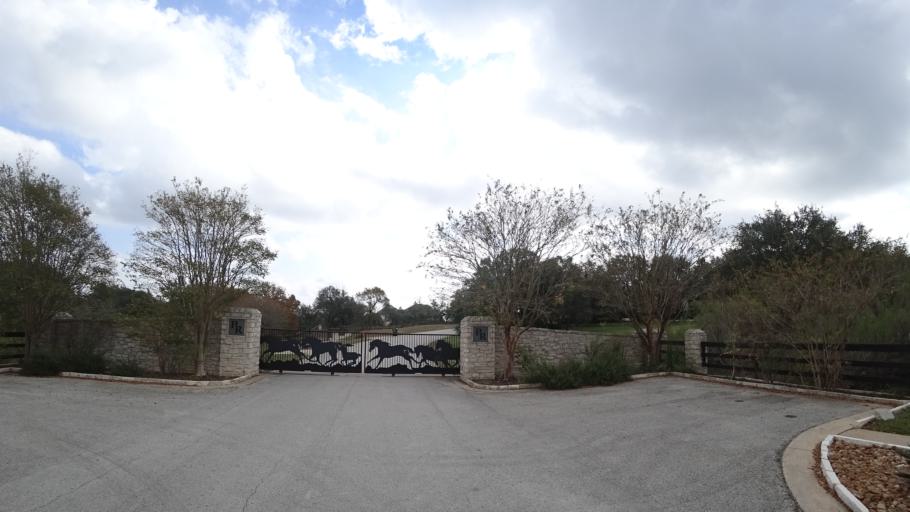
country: US
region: Texas
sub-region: Travis County
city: Barton Creek
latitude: 30.3101
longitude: -97.8862
